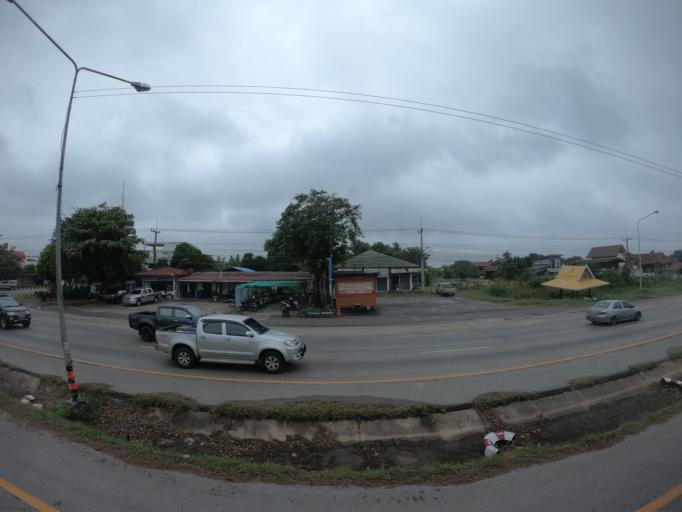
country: TH
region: Nakhon Ratchasima
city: Non Daeng
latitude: 15.3441
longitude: 102.4441
